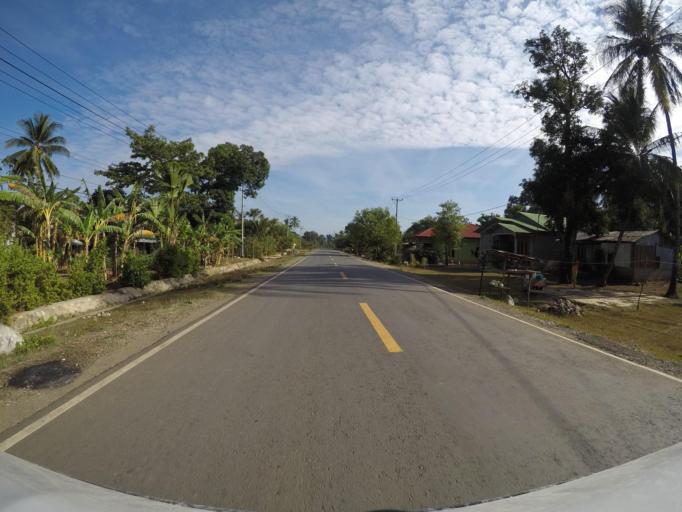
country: TL
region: Bobonaro
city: Maliana
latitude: -8.9697
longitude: 125.2182
